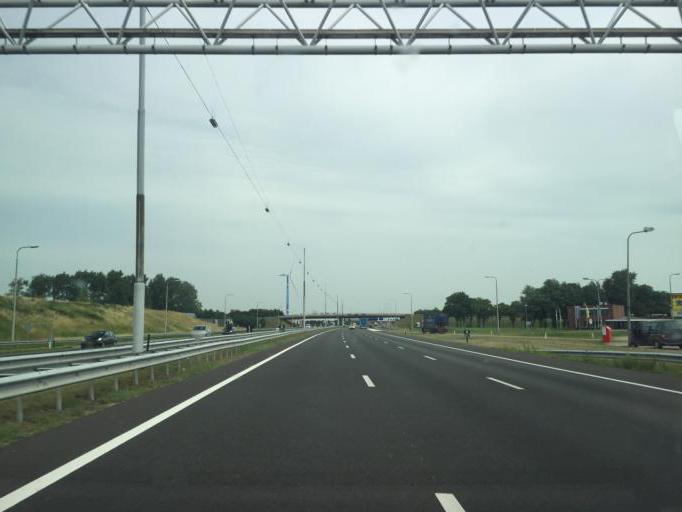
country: NL
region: North Holland
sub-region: Gemeente Uitgeest
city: Uitgeest
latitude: 52.4996
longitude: 4.7007
